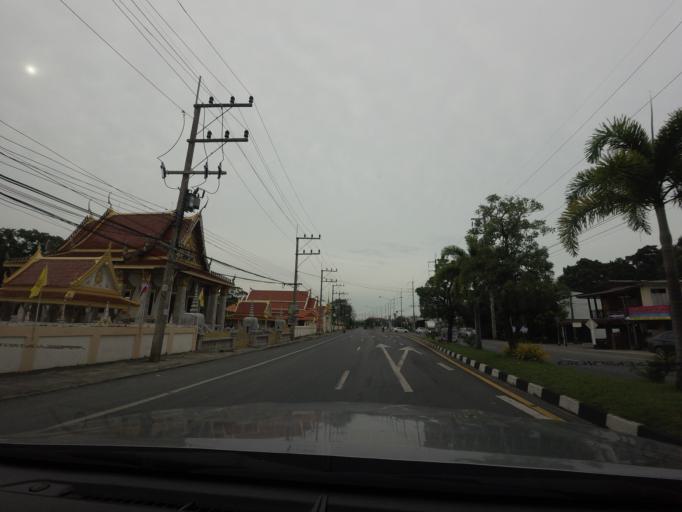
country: TH
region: Songkhla
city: Sathing Phra
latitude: 7.4741
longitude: 100.4394
